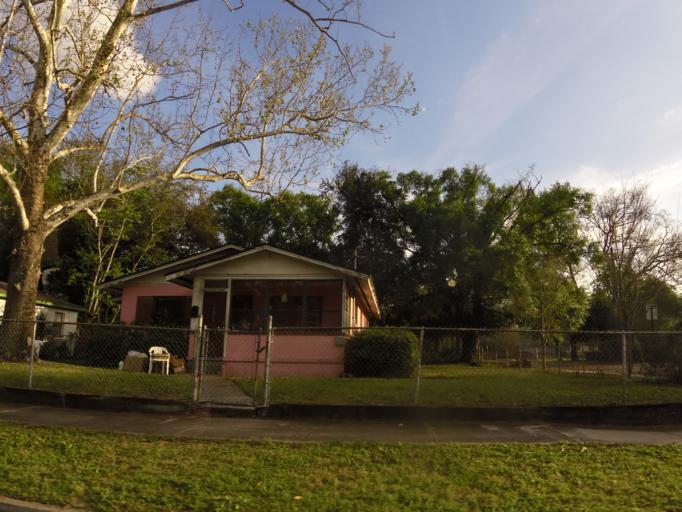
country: US
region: Florida
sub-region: Duval County
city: Jacksonville
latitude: 30.3499
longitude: -81.6885
